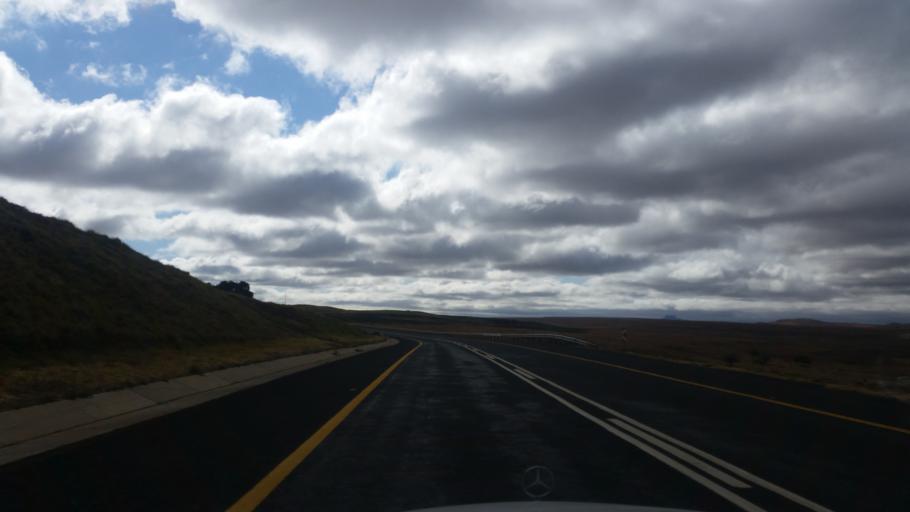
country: ZA
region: Orange Free State
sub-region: Thabo Mofutsanyana District Municipality
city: Phuthaditjhaba
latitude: -28.3121
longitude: 28.7652
